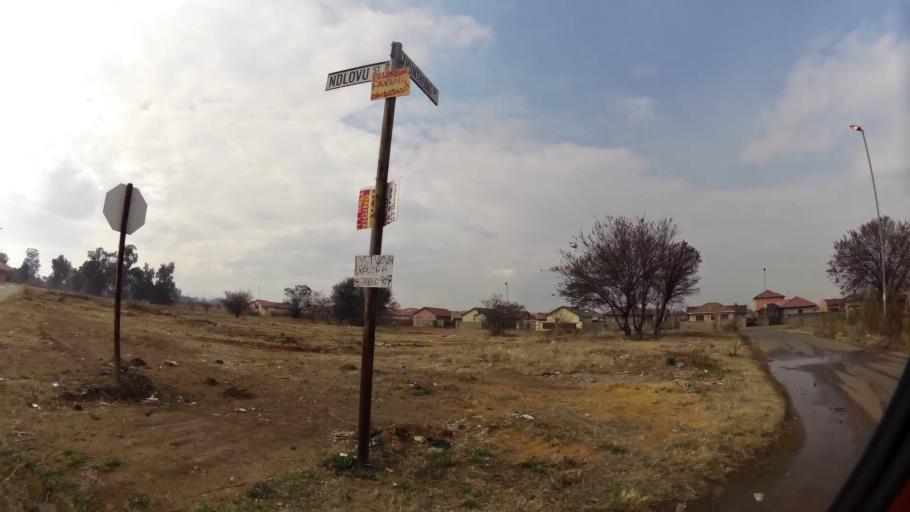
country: ZA
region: Gauteng
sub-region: Sedibeng District Municipality
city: Vanderbijlpark
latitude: -26.6822
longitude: 27.8440
